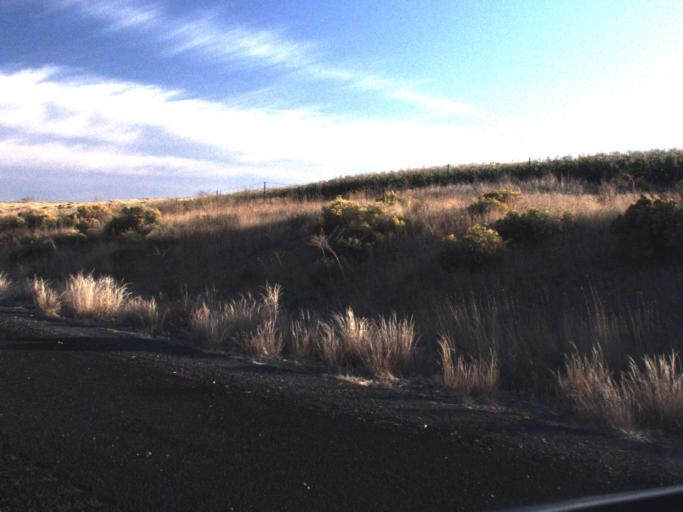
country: US
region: Washington
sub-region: Franklin County
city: Pasco
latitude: 46.2891
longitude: -119.0934
